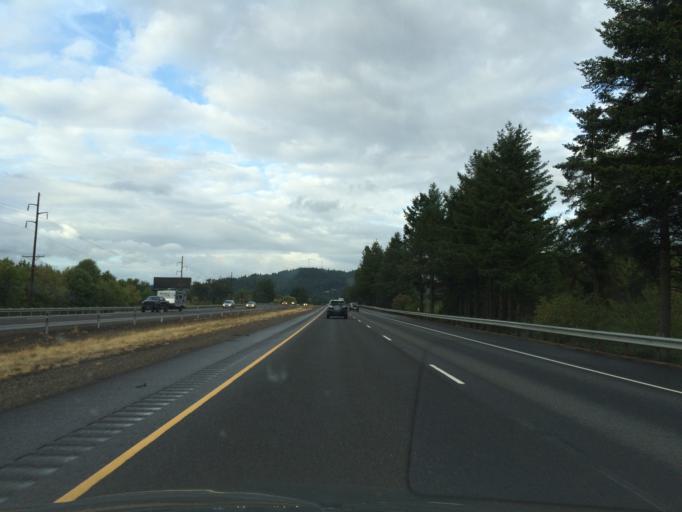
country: US
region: Oregon
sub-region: Lane County
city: Cottage Grove
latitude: 43.7635
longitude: -123.0779
